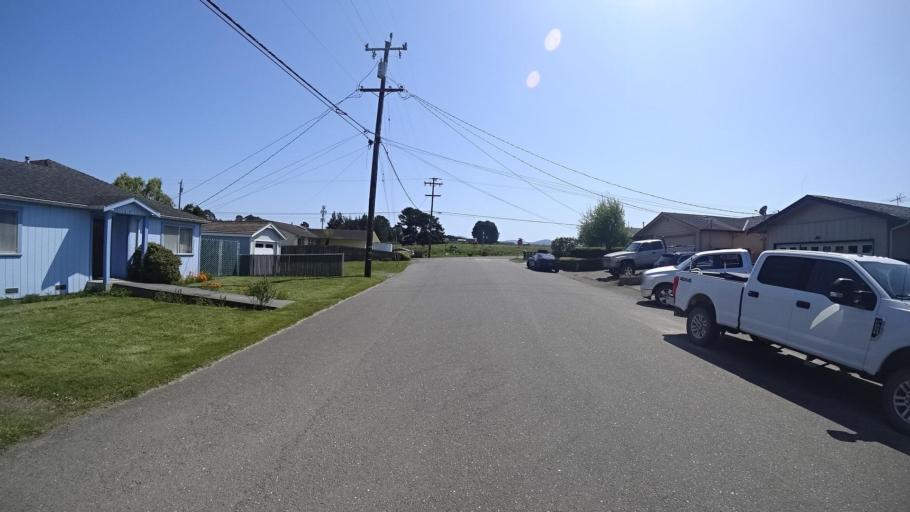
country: US
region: California
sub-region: Humboldt County
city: Hydesville
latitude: 40.5635
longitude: -124.1339
